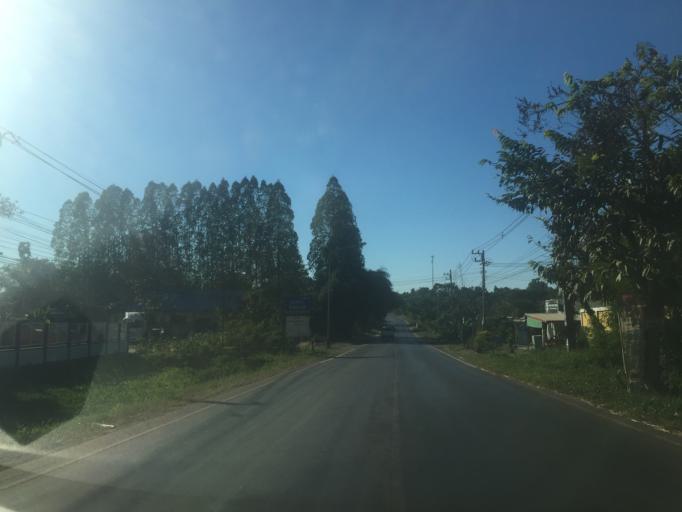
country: TH
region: Changwat Udon Thani
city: Si That
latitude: 16.9746
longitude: 103.2090
